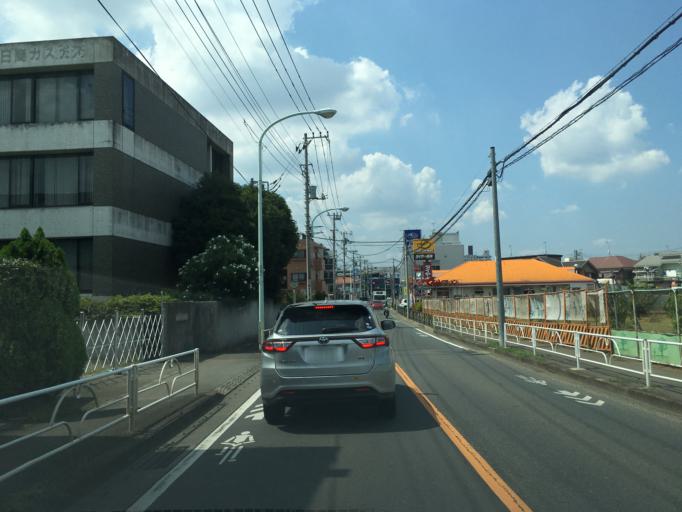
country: JP
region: Tokyo
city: Higashimurayama-shi
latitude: 35.7659
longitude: 139.4911
